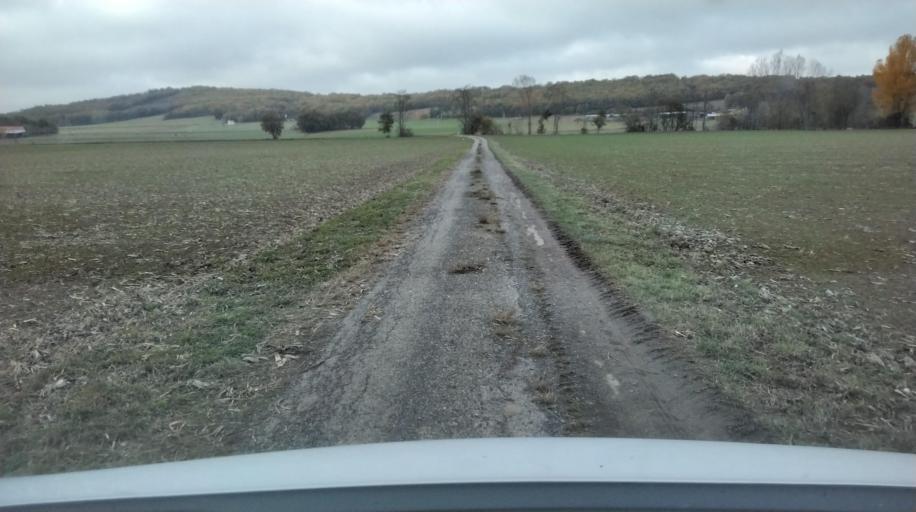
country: FR
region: Midi-Pyrenees
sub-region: Departement de la Haute-Garonne
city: Le Fousseret
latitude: 43.2688
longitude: 1.0438
